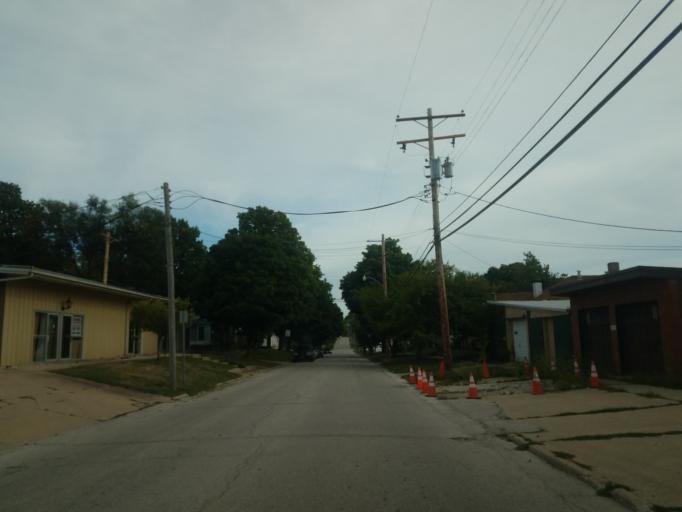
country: US
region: Illinois
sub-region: McLean County
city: Bloomington
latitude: 40.4779
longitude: -88.9800
